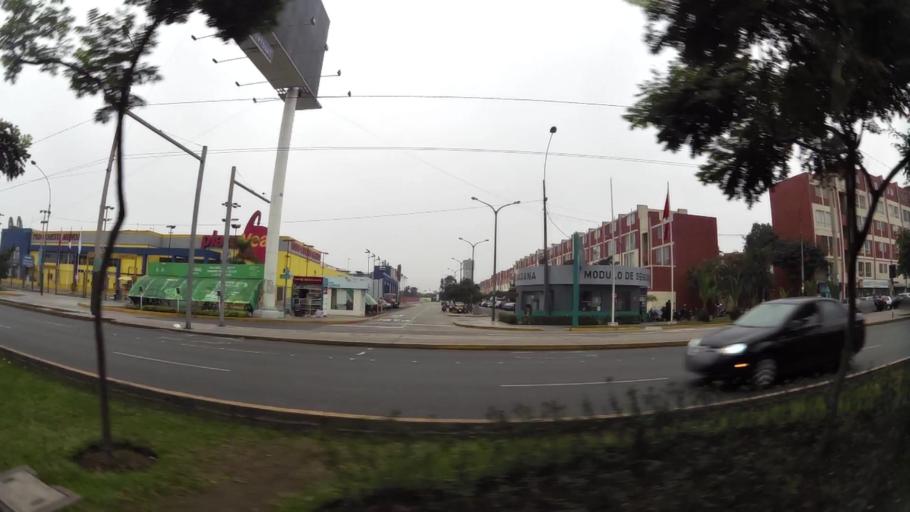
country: PE
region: Lima
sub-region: Lima
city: Surco
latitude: -12.1122
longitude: -77.0060
